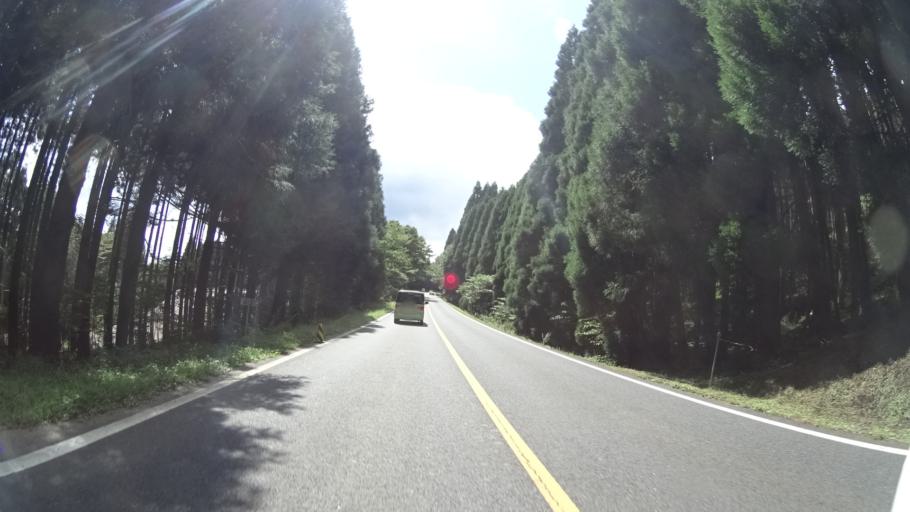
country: JP
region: Oita
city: Tsukawaki
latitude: 33.2155
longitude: 131.2975
